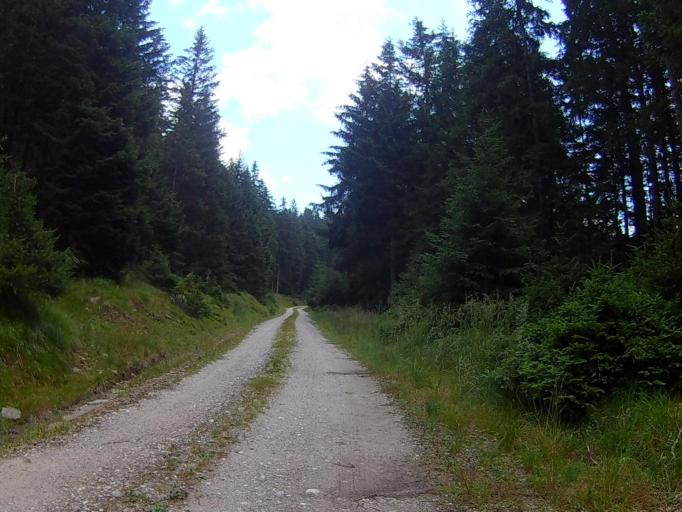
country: SI
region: Lovrenc na Pohorju
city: Lovrenc na Pohorju
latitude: 46.4829
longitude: 15.3999
